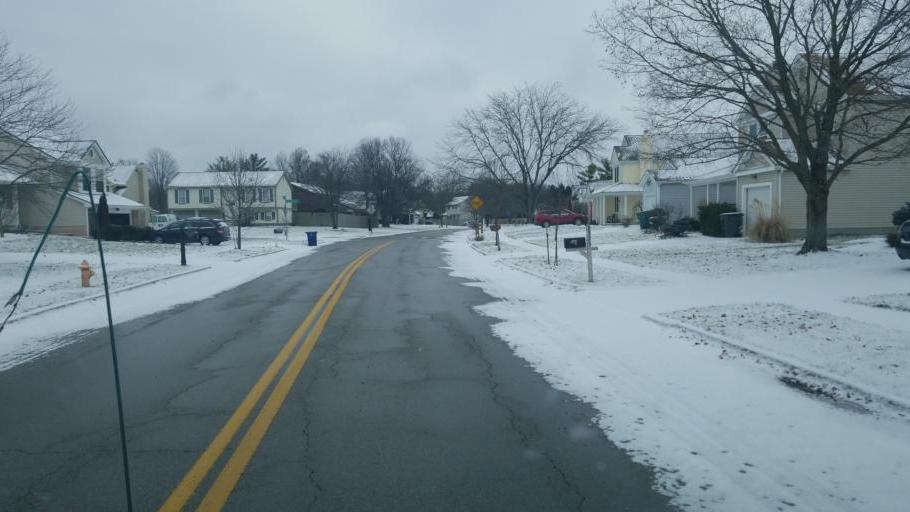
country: US
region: Ohio
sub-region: Franklin County
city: Dublin
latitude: 40.1140
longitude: -83.0792
